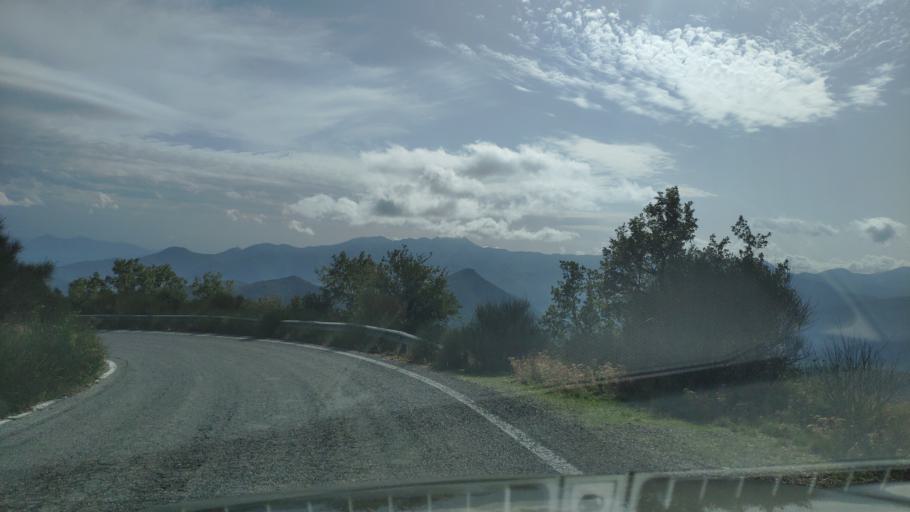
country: GR
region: Peloponnese
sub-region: Nomos Arkadias
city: Dimitsana
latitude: 37.5734
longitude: 22.0190
